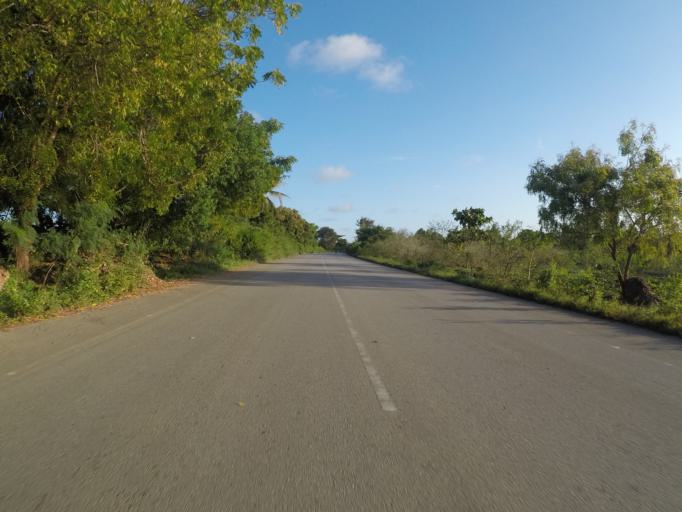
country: TZ
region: Zanzibar North
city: Kijini
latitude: -5.8428
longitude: 39.2839
